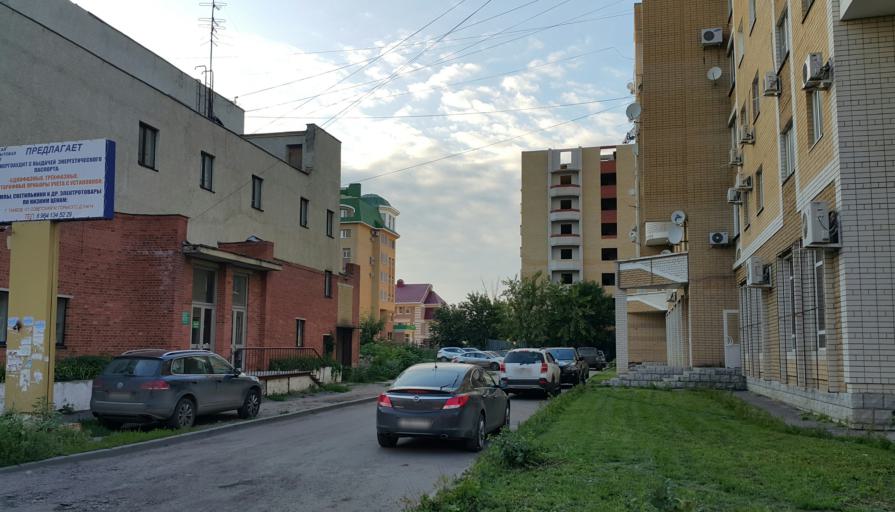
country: RU
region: Tambov
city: Tambov
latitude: 52.7203
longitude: 41.4411
